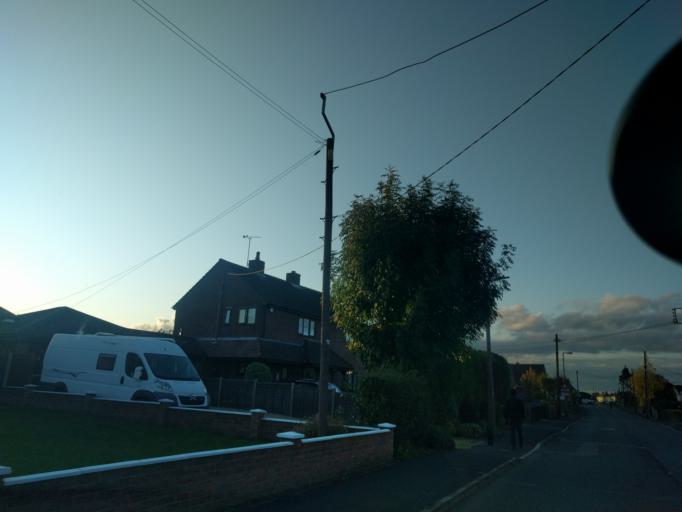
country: GB
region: England
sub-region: Essex
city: Rayne
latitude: 51.8739
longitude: 0.5768
